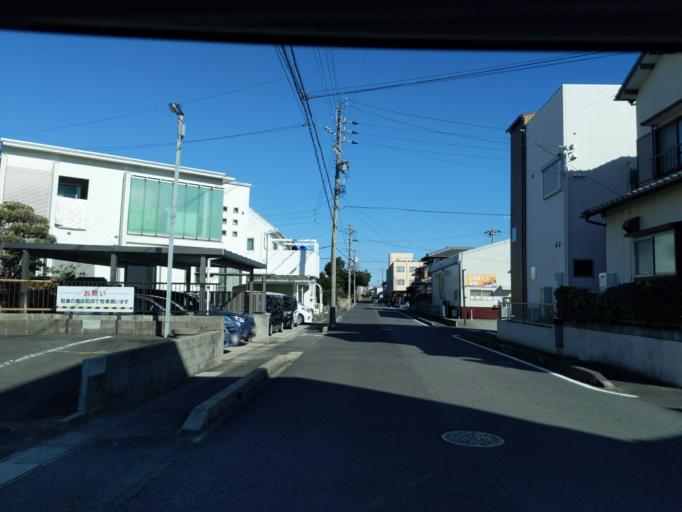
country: JP
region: Aichi
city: Kasugai
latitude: 35.2539
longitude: 136.9721
